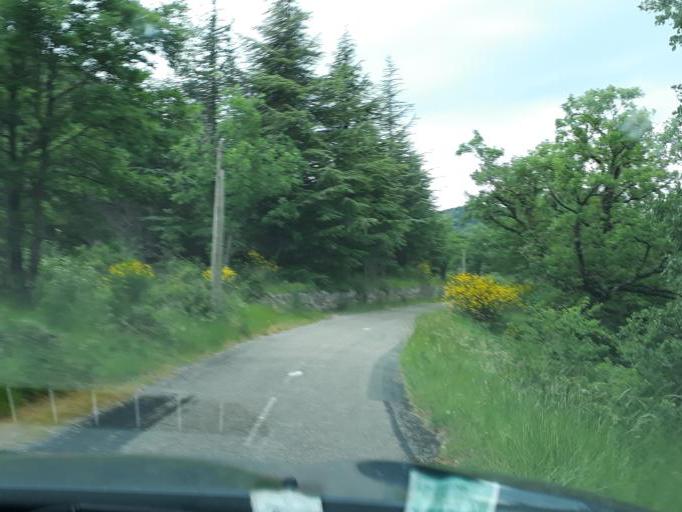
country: FR
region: Languedoc-Roussillon
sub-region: Departement de l'Herault
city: Lodeve
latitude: 43.7865
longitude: 3.2825
